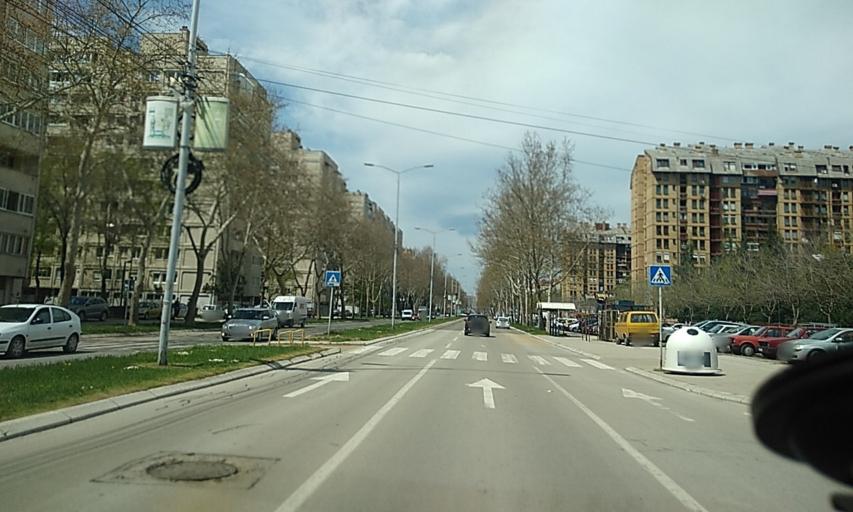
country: RS
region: Central Serbia
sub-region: Nisavski Okrug
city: Nis
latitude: 43.3176
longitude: 21.9233
